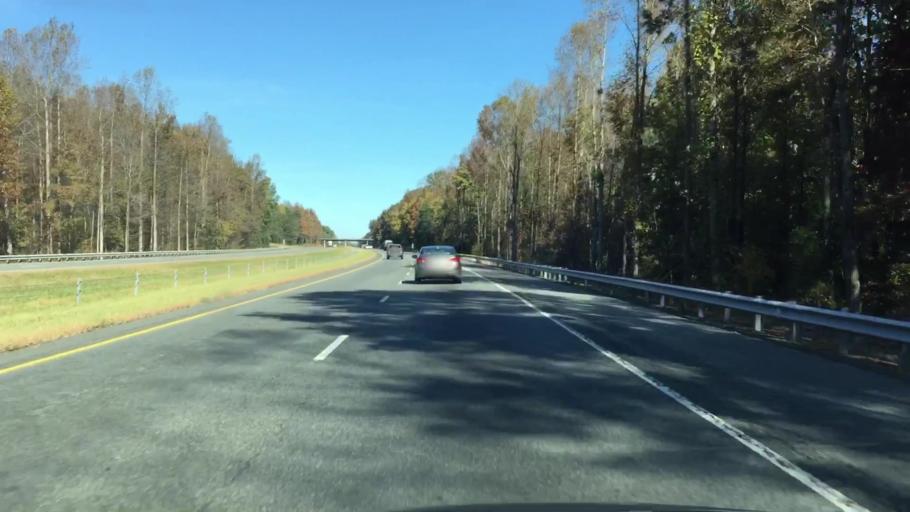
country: US
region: North Carolina
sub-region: Rockingham County
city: Reidsville
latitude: 36.2797
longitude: -79.6399
